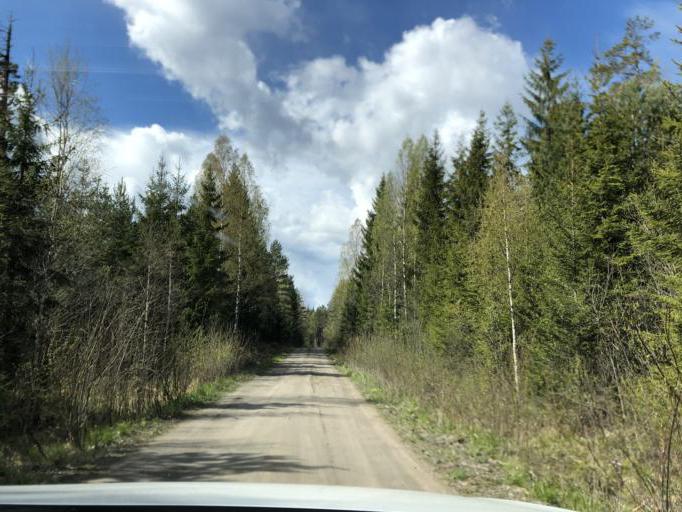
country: SE
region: Uppsala
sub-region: Heby Kommun
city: Tarnsjo
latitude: 60.2524
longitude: 16.9057
